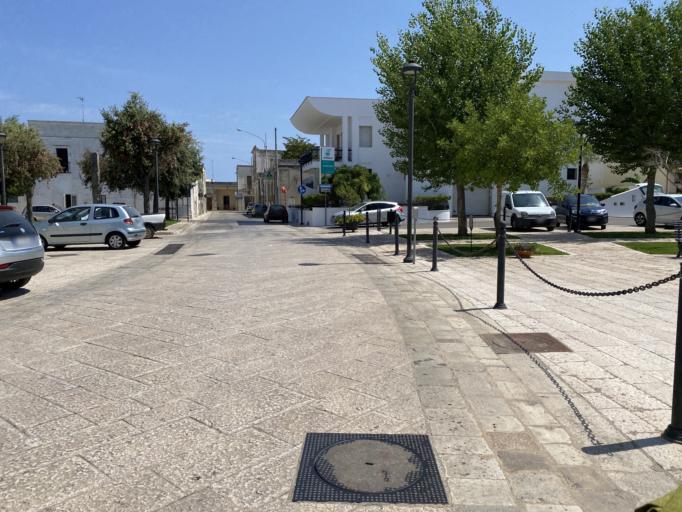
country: IT
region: Apulia
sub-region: Provincia di Lecce
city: Muro Leccese
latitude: 40.0977
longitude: 18.3392
